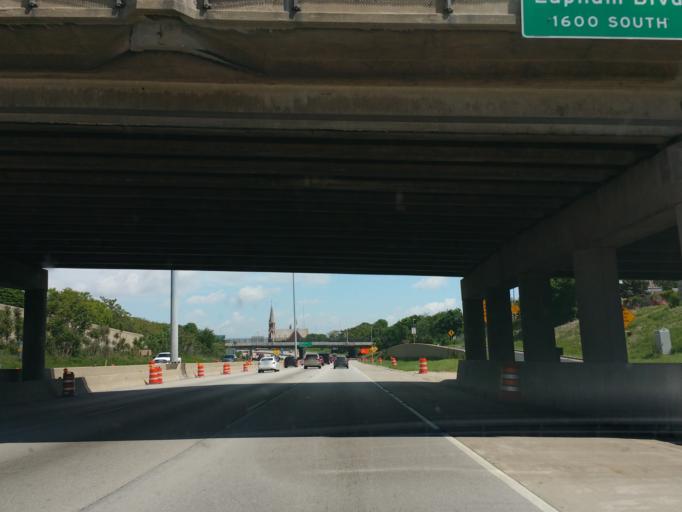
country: US
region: Wisconsin
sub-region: Milwaukee County
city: Milwaukee
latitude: 43.0139
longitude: -87.9159
